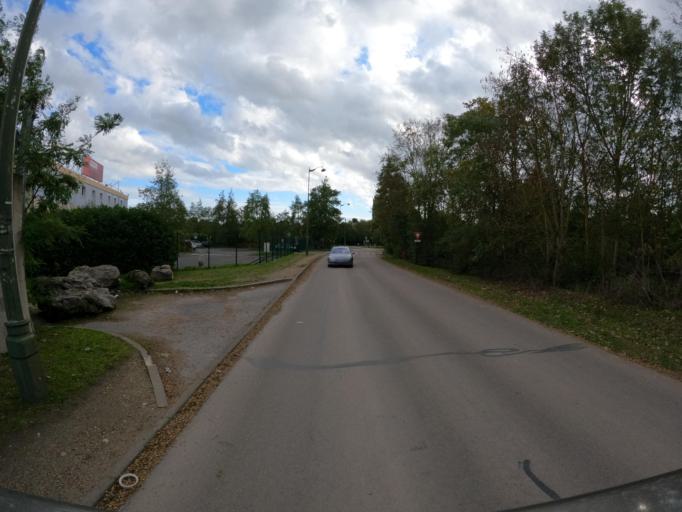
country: FR
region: Ile-de-France
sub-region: Departement de Seine-et-Marne
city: Esbly
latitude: 48.9141
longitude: 2.8150
